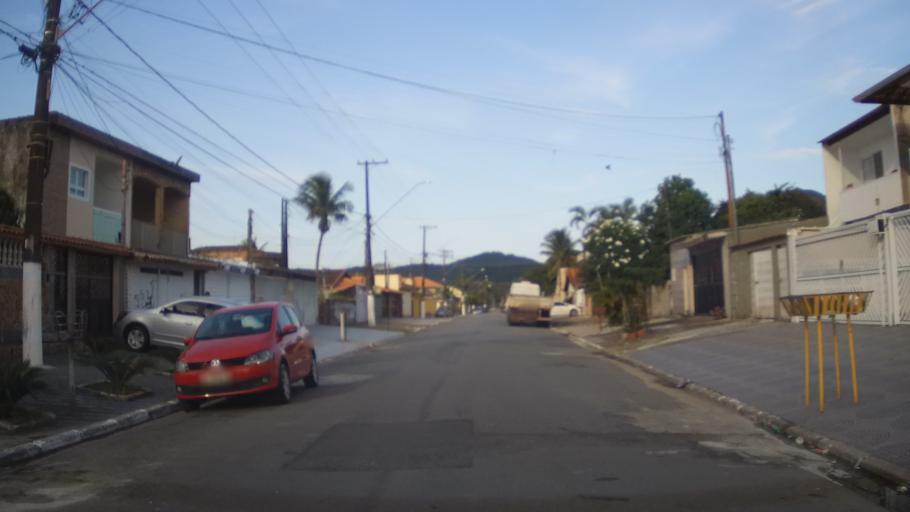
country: BR
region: Sao Paulo
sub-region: Praia Grande
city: Praia Grande
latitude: -23.9983
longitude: -46.4190
